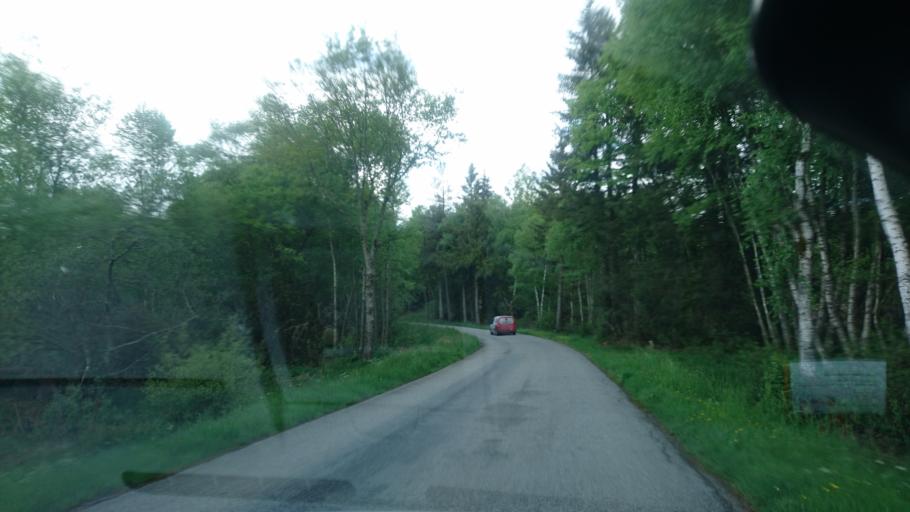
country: FR
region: Limousin
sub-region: Departement de la Haute-Vienne
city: Peyrat-le-Chateau
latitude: 45.7920
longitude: 1.9214
